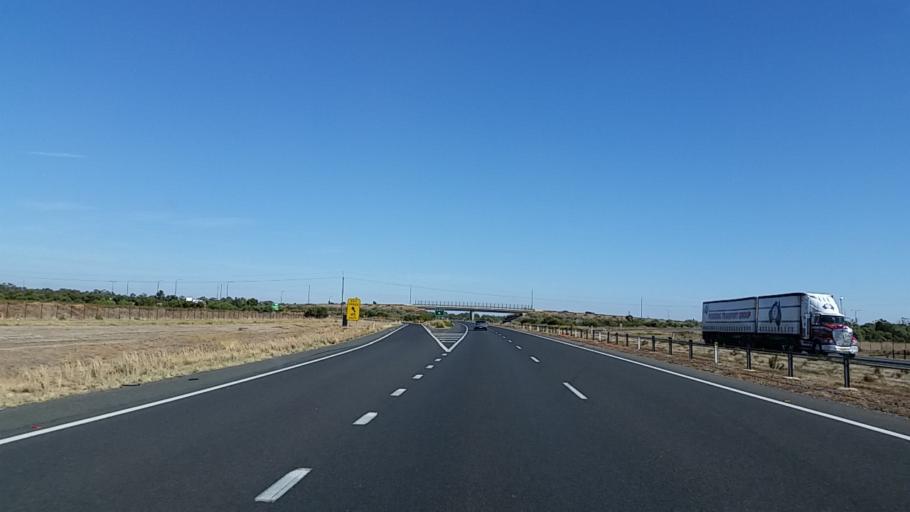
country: AU
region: South Australia
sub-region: Playford
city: Angle Vale
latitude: -34.6593
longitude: 138.6570
